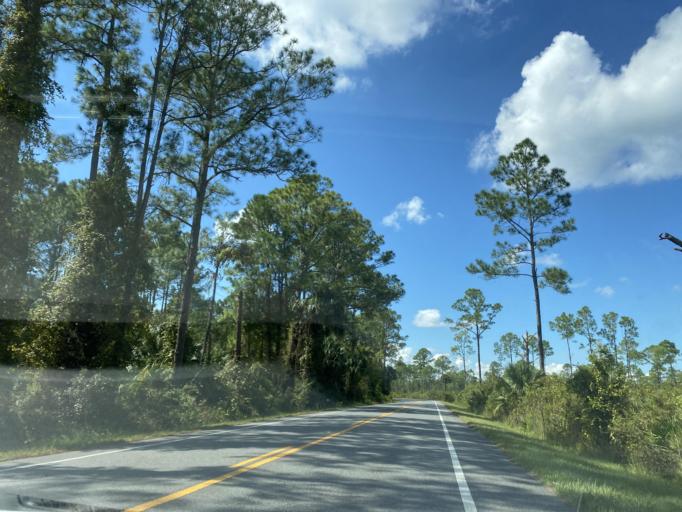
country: US
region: Florida
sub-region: Lake County
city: Lake Mack-Forest Hills
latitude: 29.0163
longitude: -81.4713
